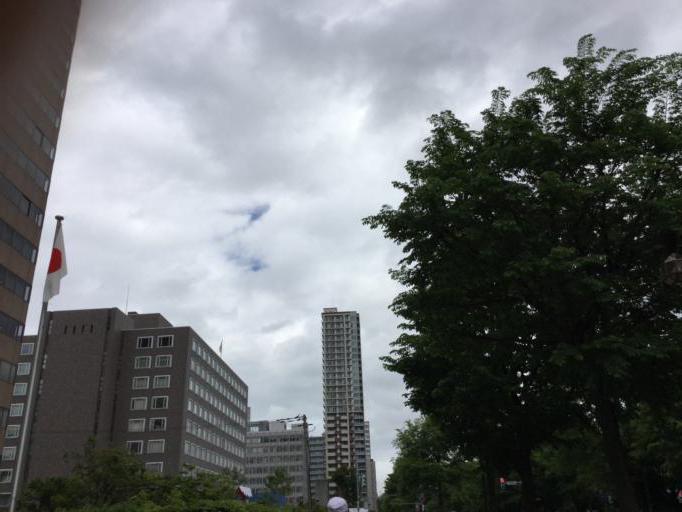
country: JP
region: Hokkaido
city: Sapporo
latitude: 43.0592
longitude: 141.3386
